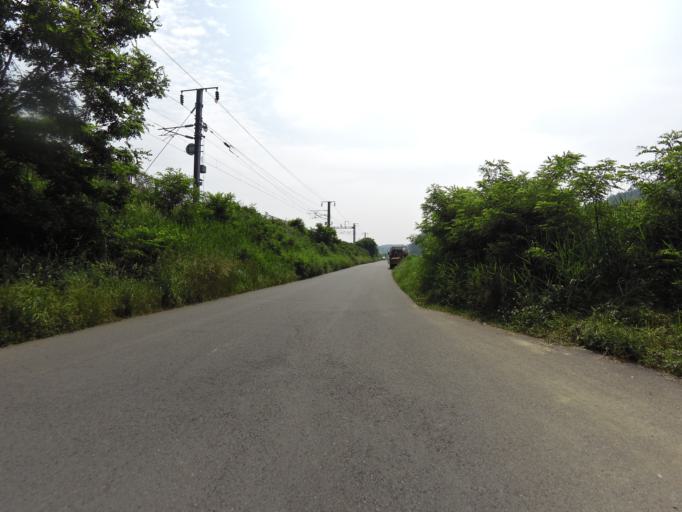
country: KR
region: Gyeongsangbuk-do
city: Gyeongsan-si
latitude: 35.8521
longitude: 128.7008
